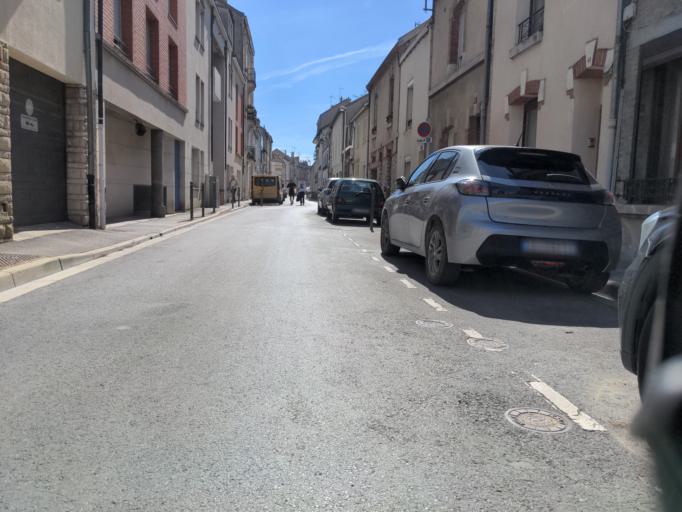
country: FR
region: Champagne-Ardenne
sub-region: Departement de la Marne
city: Reims
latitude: 49.2585
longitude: 4.0494
